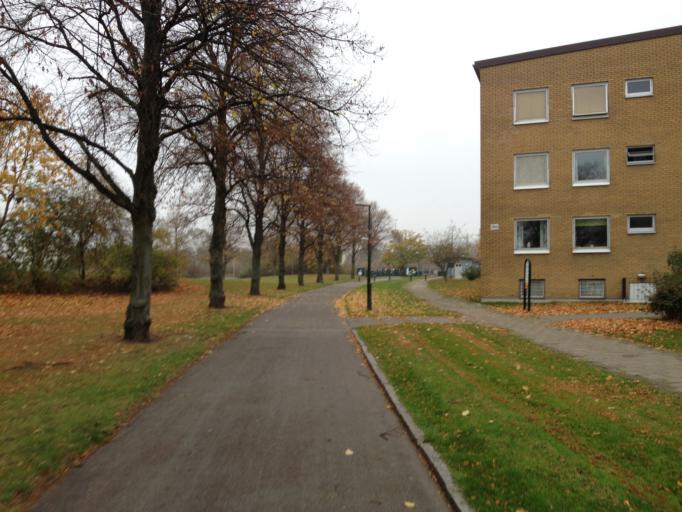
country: SE
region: Skane
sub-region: Burlovs Kommun
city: Arloev
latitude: 55.6181
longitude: 13.0571
